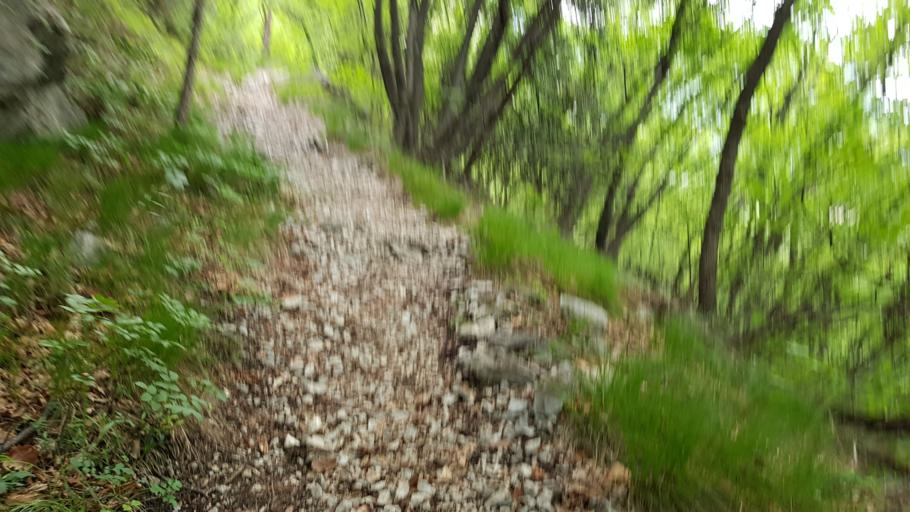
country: IT
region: Trentino-Alto Adige
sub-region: Provincia di Trento
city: Padergnone
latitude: 46.0717
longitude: 10.9806
